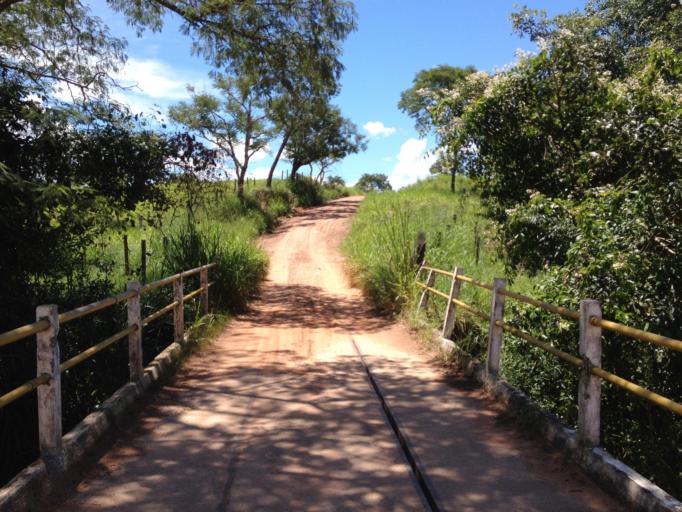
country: BR
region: Goias
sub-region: Ipameri
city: Ipameri
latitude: -17.9729
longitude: -48.1776
